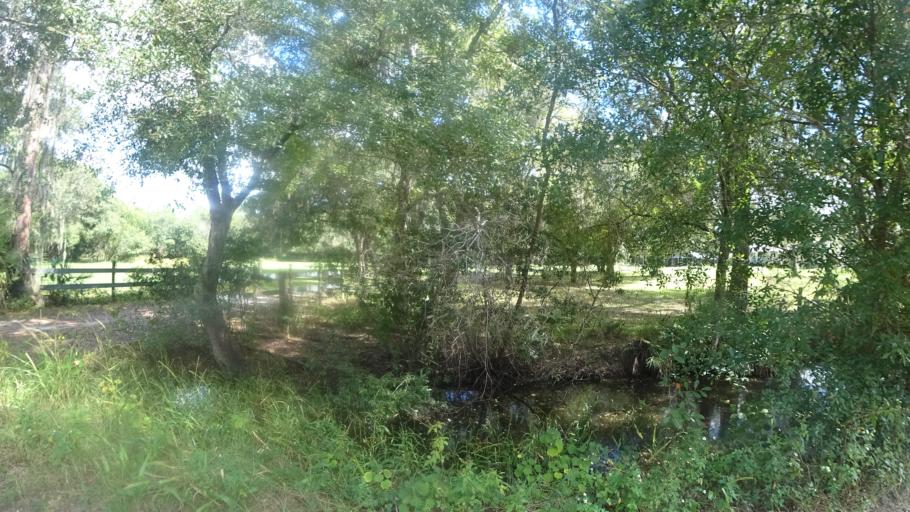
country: US
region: Florida
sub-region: Hillsborough County
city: Sun City Center
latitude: 27.6322
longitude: -82.3651
